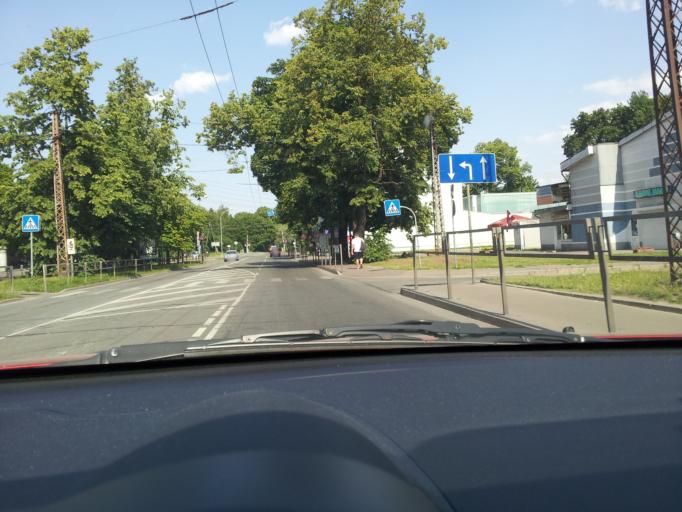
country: LV
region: Riga
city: Riga
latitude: 56.9952
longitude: 24.1284
